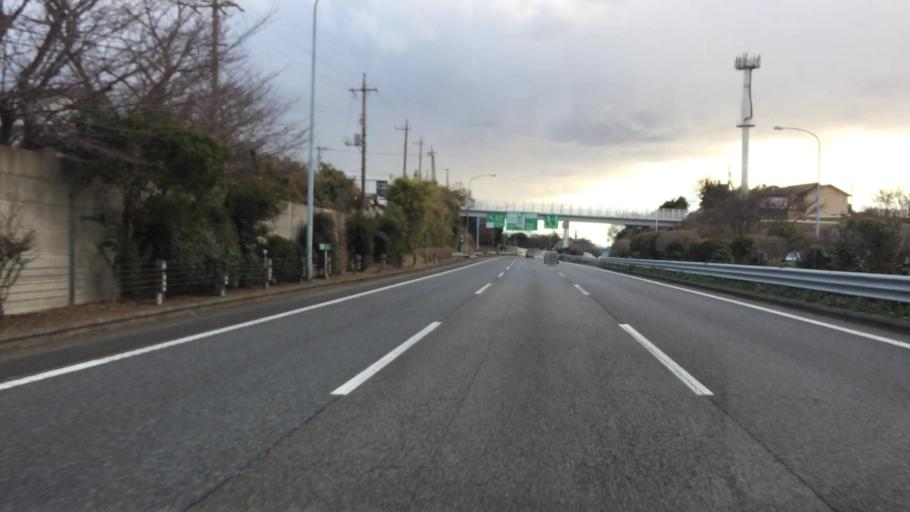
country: JP
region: Kanagawa
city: Yokohama
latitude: 35.4959
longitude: 139.5917
